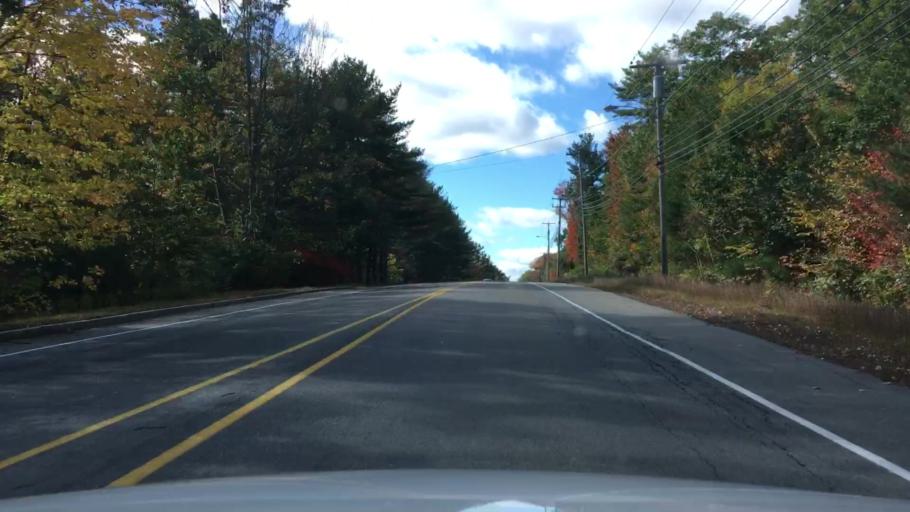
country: US
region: Maine
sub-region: York County
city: Biddeford
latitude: 43.4753
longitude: -70.5148
